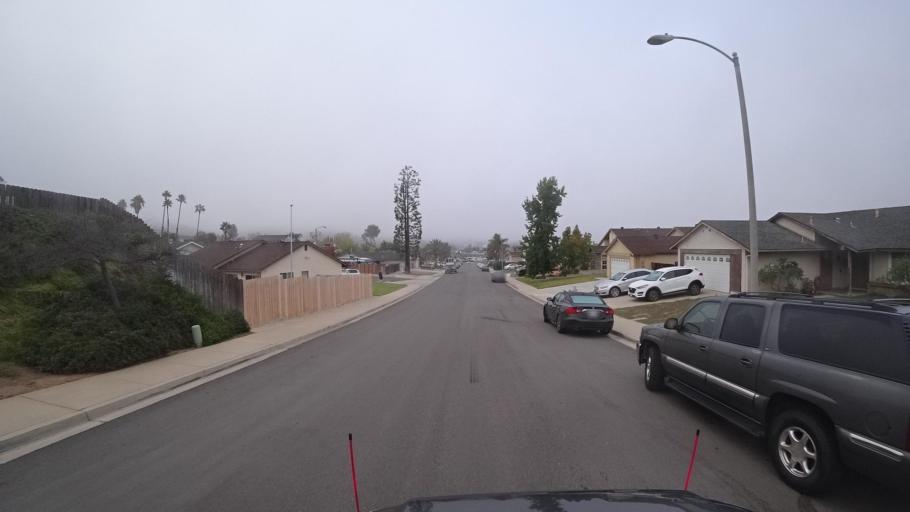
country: US
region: California
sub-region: San Diego County
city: Rancho San Diego
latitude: 32.7315
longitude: -116.9570
